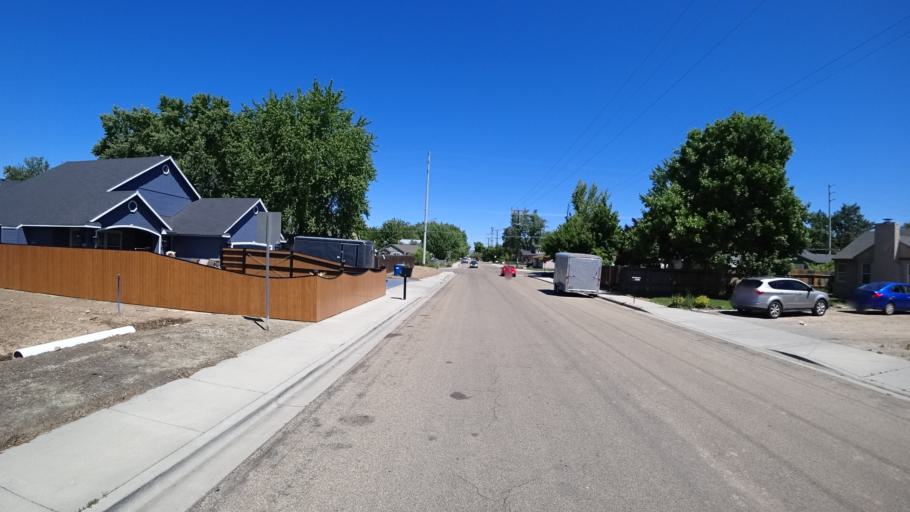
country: US
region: Idaho
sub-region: Ada County
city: Garden City
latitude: 43.5867
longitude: -116.2287
